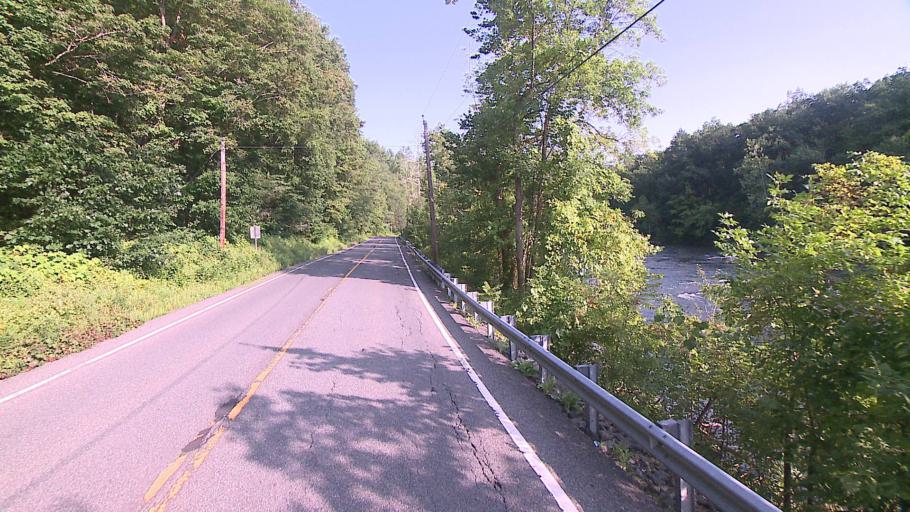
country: US
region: Connecticut
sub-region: Litchfield County
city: Kent
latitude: 41.8287
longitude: -73.3832
